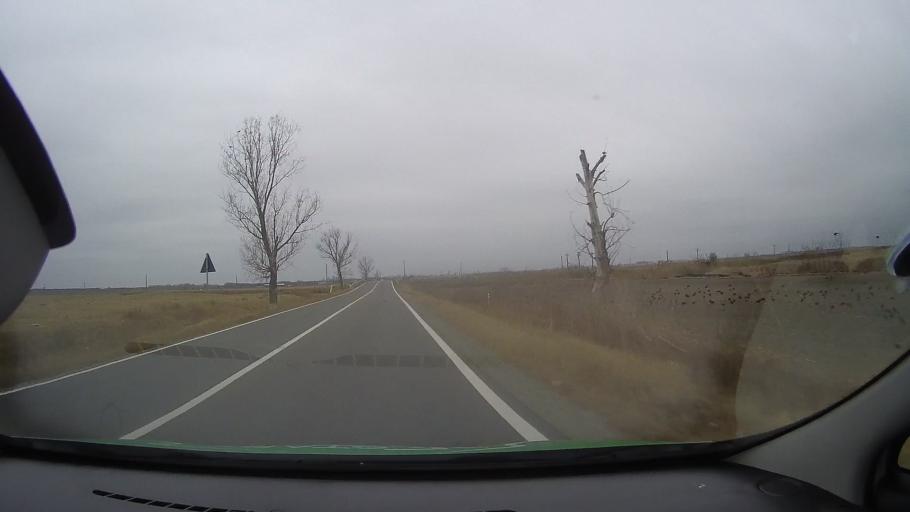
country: RO
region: Ialomita
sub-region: Comuna Slobozia
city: Slobozia
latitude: 44.5918
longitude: 27.3906
